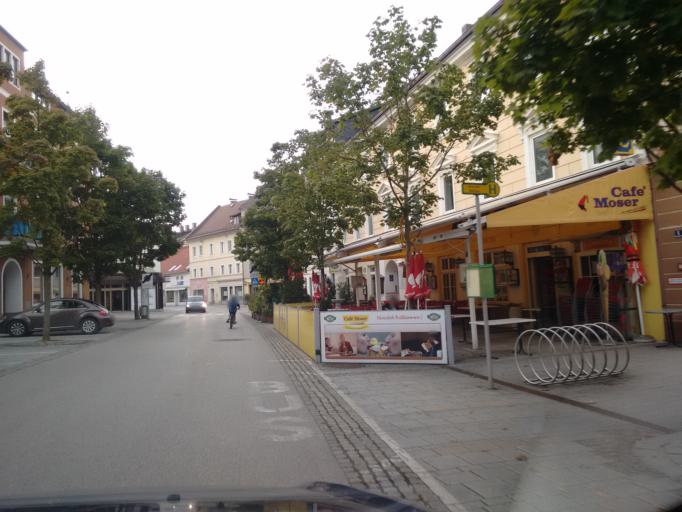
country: AT
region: Upper Austria
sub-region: Politischer Bezirk Steyr-Land
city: Bad Hall
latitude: 48.0351
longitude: 14.2084
